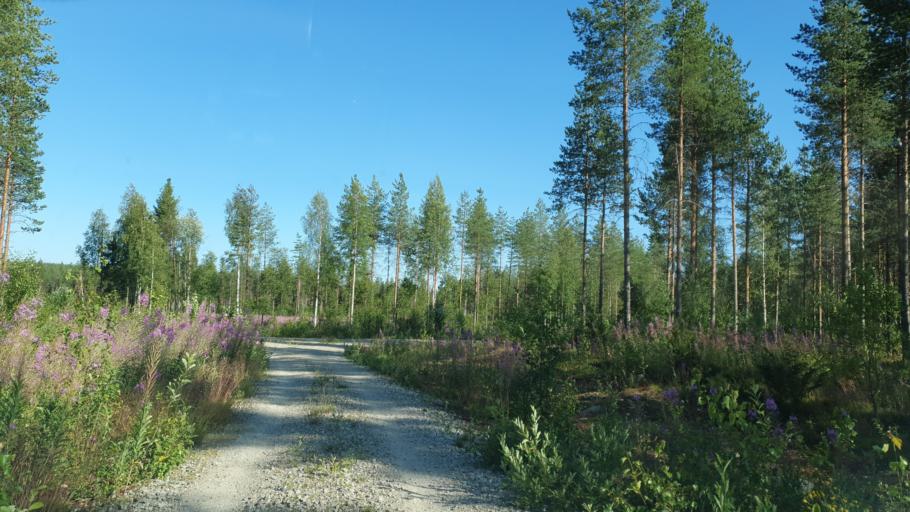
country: FI
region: Kainuu
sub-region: Kehys-Kainuu
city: Kuhmo
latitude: 64.0019
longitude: 29.7753
